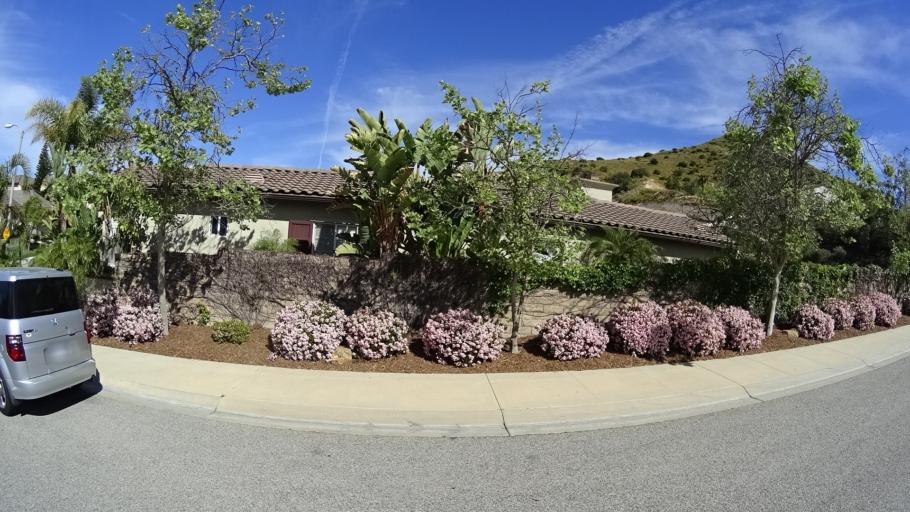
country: US
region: California
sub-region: Ventura County
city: Casa Conejo
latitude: 34.1743
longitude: -118.9684
